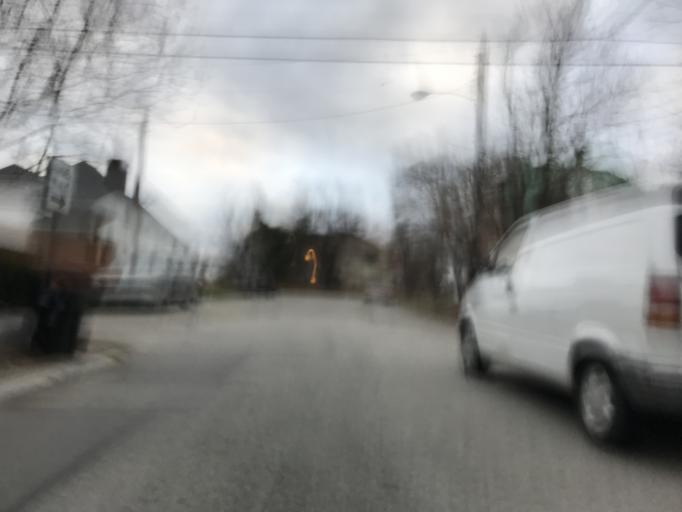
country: US
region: Kentucky
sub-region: Jefferson County
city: Louisville
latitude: 38.2345
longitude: -85.7454
